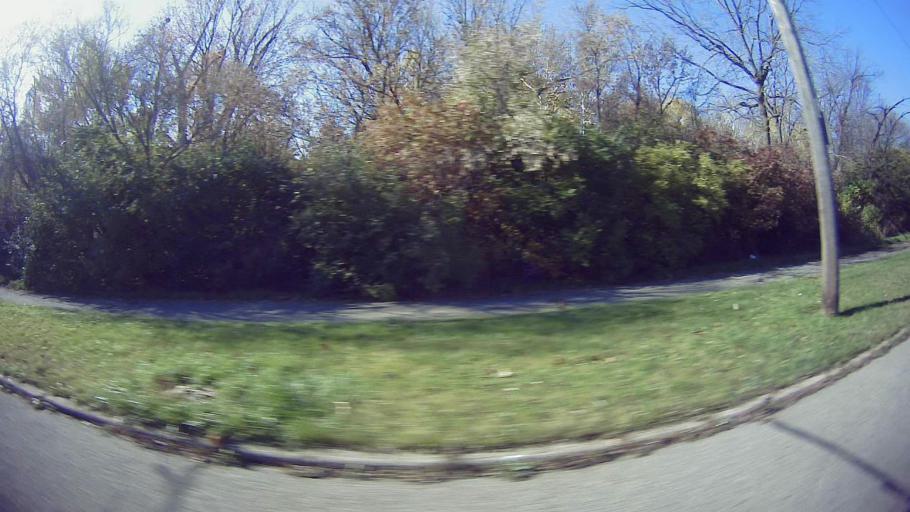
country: US
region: Michigan
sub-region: Wayne County
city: Dearborn Heights
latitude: 42.3515
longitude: -83.2482
